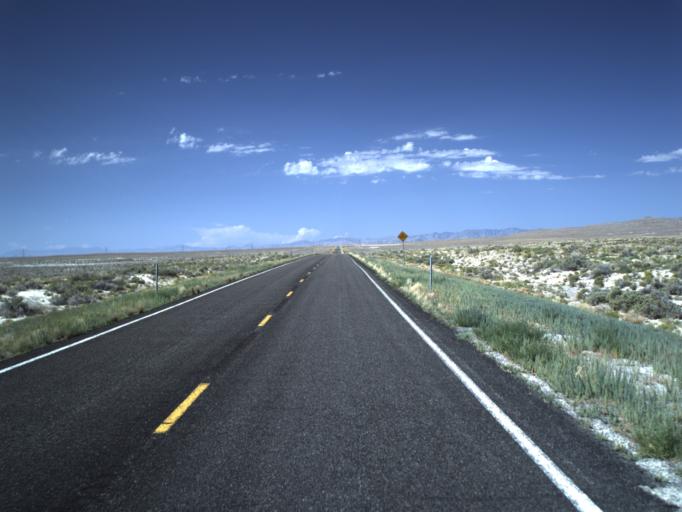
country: US
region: Utah
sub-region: Millard County
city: Delta
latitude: 39.1901
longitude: -113.0010
